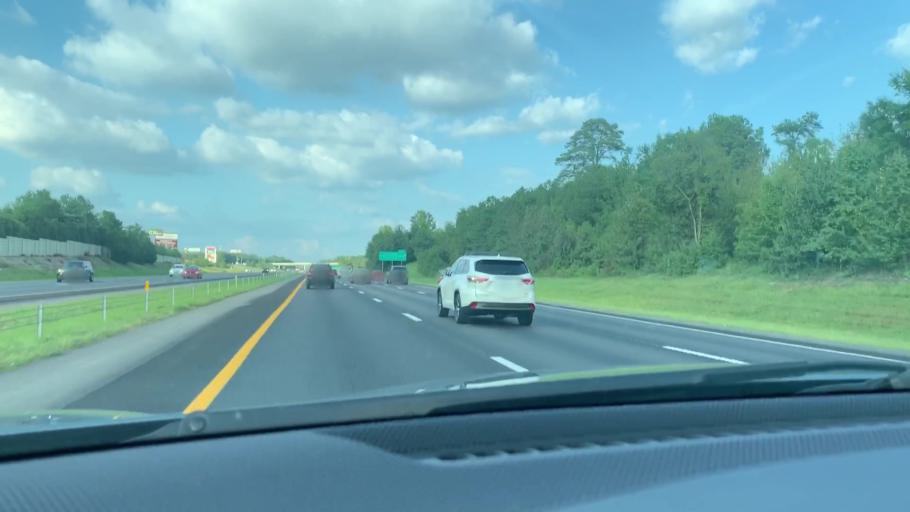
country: US
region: South Carolina
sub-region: Richland County
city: Forest Acres
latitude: 34.0147
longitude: -80.9507
